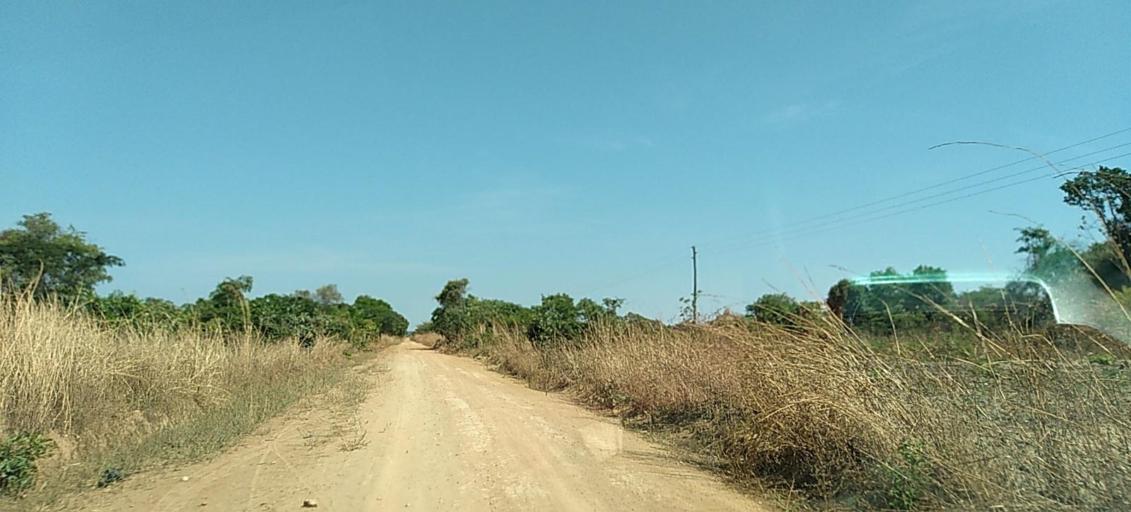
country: ZM
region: Copperbelt
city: Chililabombwe
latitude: -12.3508
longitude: 27.8824
